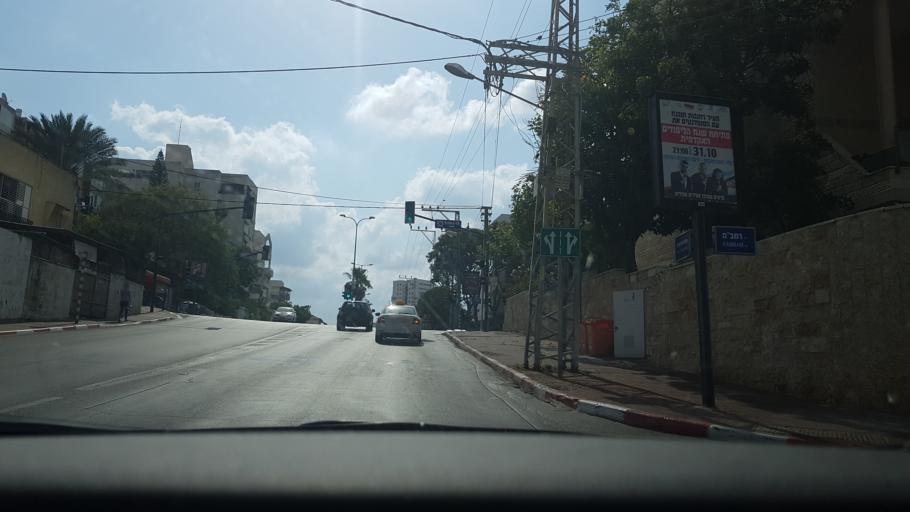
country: IL
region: Central District
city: Ness Ziona
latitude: 31.8864
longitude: 34.8080
